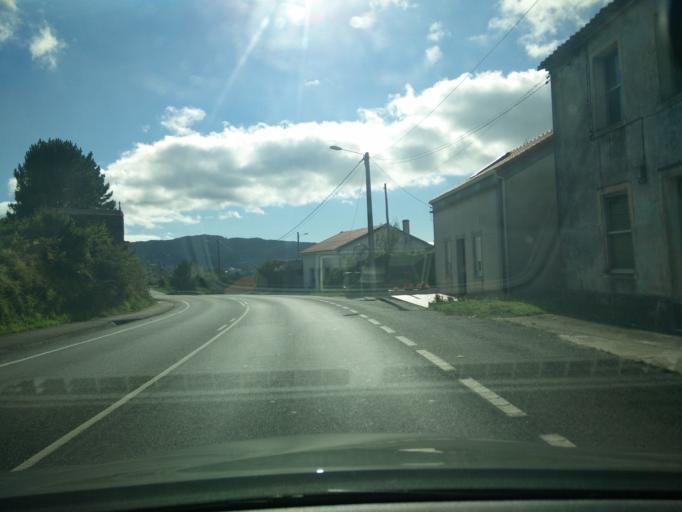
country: ES
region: Galicia
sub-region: Provincia da Coruna
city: Laxe
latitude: 43.2229
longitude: -8.9217
